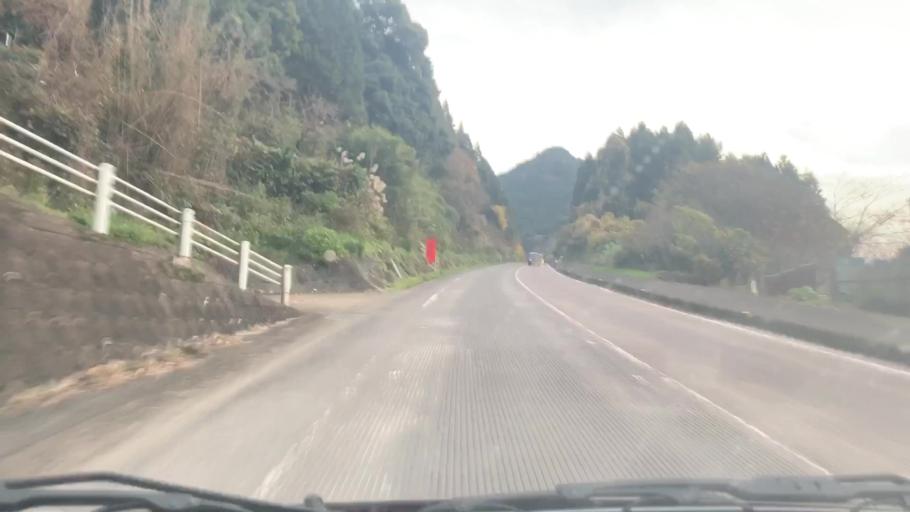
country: JP
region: Saga Prefecture
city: Kashima
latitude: 33.0554
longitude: 130.0717
